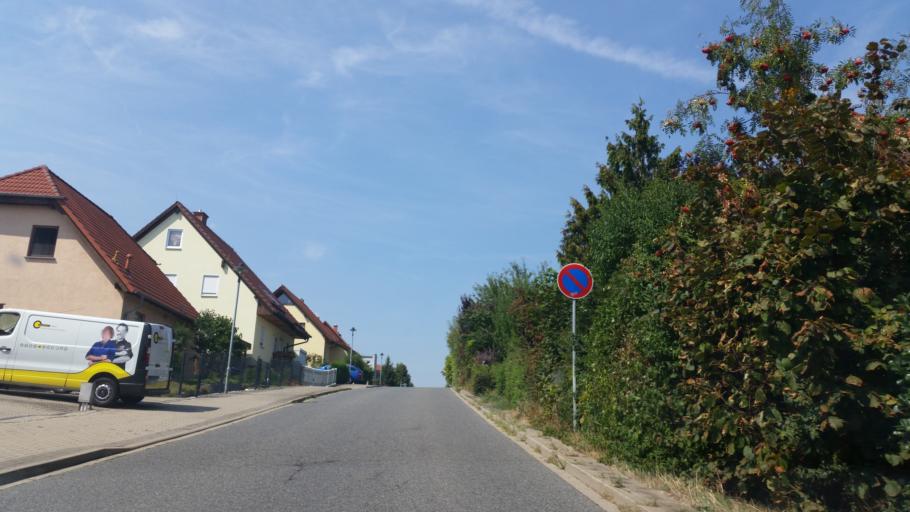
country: DE
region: Saxony
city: Klipphausen
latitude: 51.0721
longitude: 13.5286
